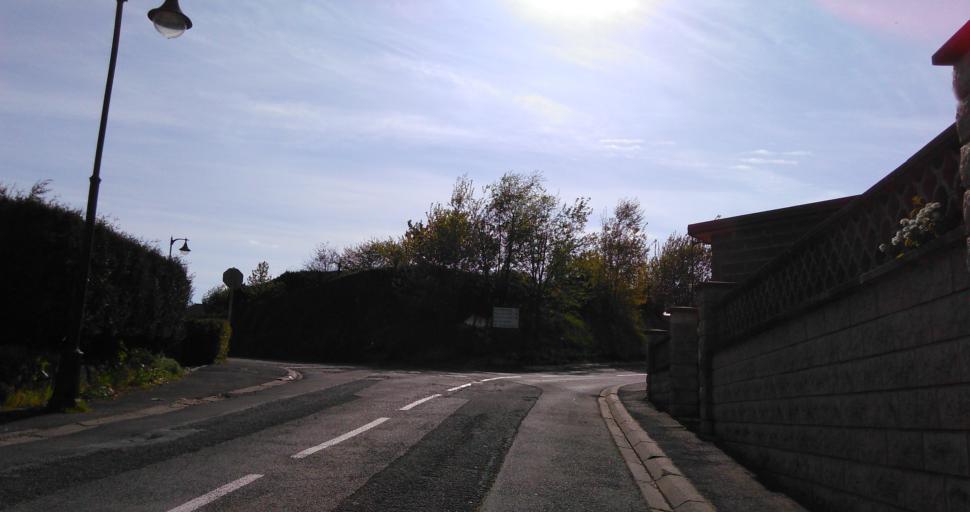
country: LU
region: Luxembourg
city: Belvaux
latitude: 49.4976
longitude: 5.9171
